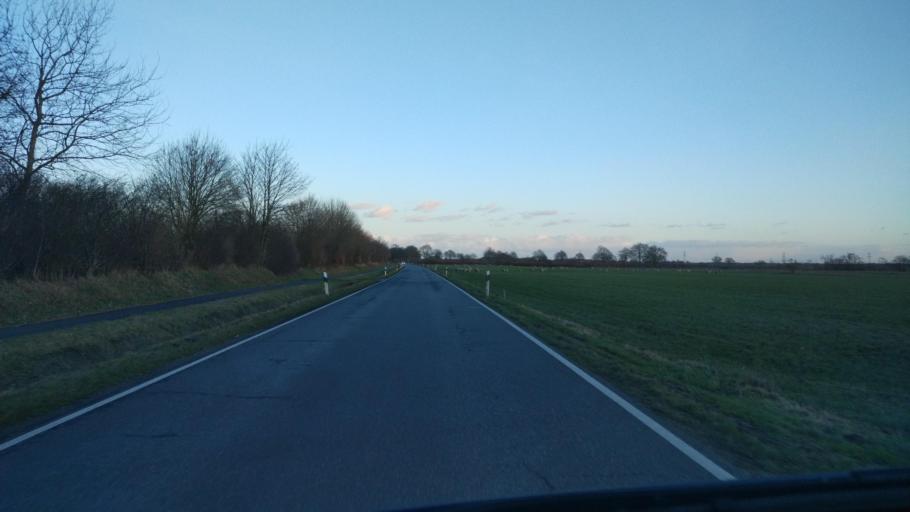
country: DE
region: Schleswig-Holstein
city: Ellingstedt
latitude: 54.4657
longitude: 9.3807
